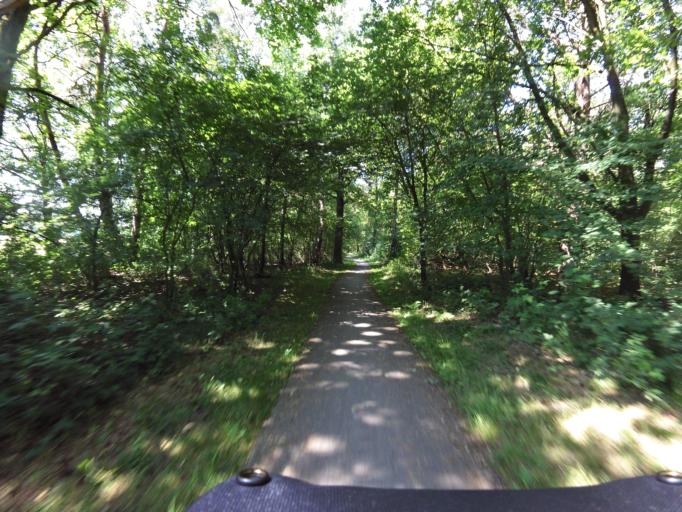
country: NL
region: Overijssel
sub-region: Gemeente Twenterand
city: Den Ham
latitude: 52.4885
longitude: 6.4776
